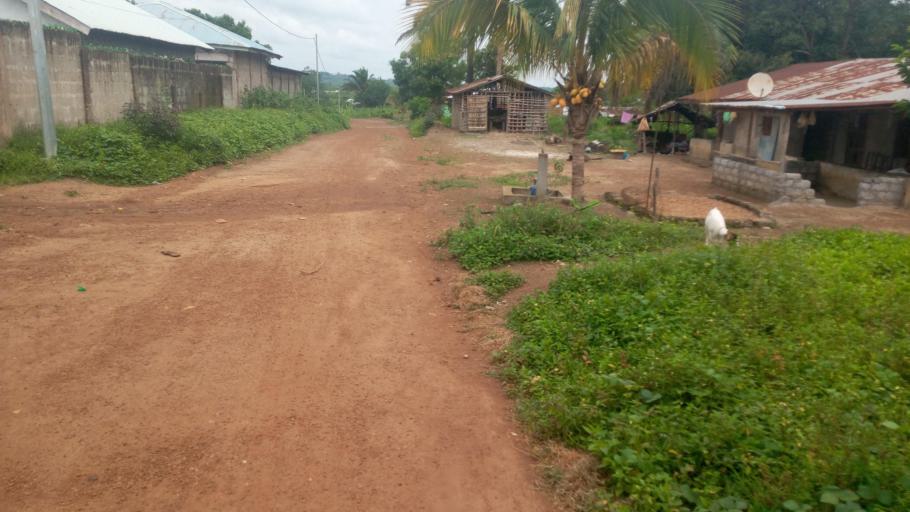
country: SL
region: Southern Province
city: Mogbwemo
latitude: 7.7832
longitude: -12.2998
